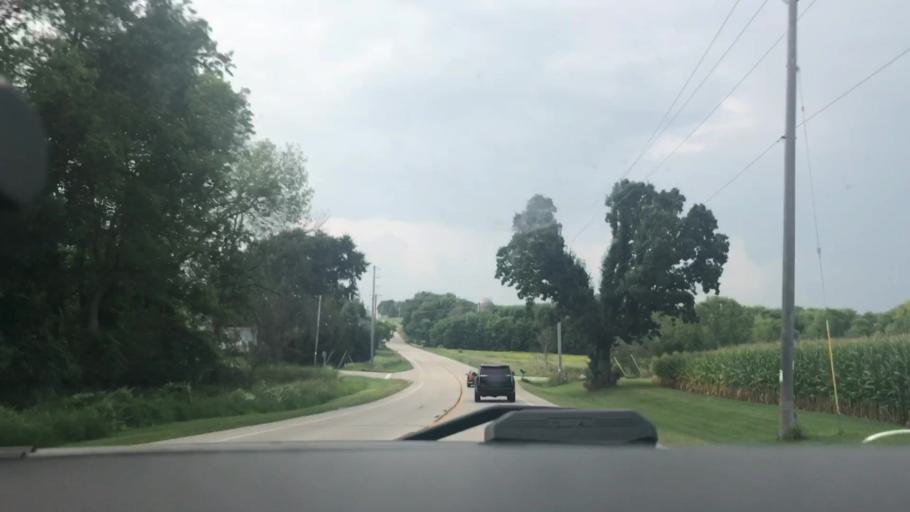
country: US
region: Wisconsin
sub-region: Washington County
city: Hartford
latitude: 43.3981
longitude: -88.3627
